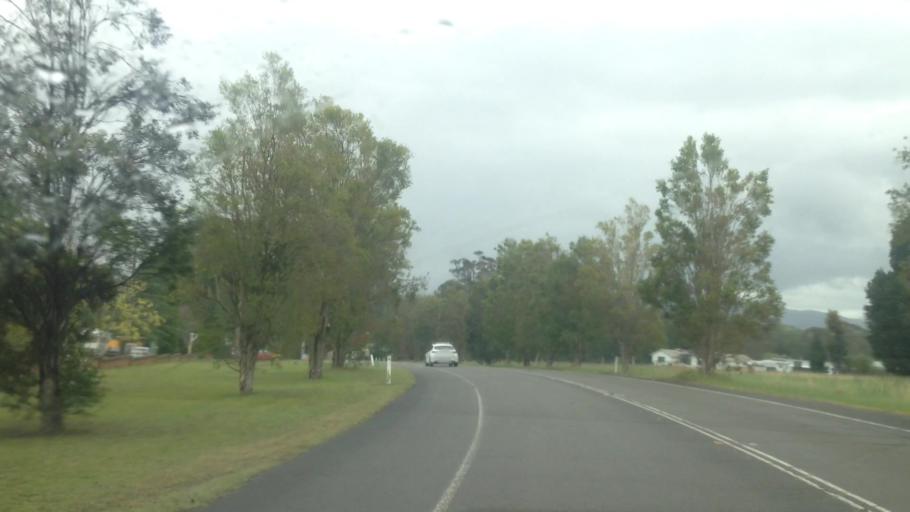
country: AU
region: New South Wales
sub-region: Lake Macquarie Shire
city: Dora Creek
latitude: -33.1029
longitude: 151.4770
